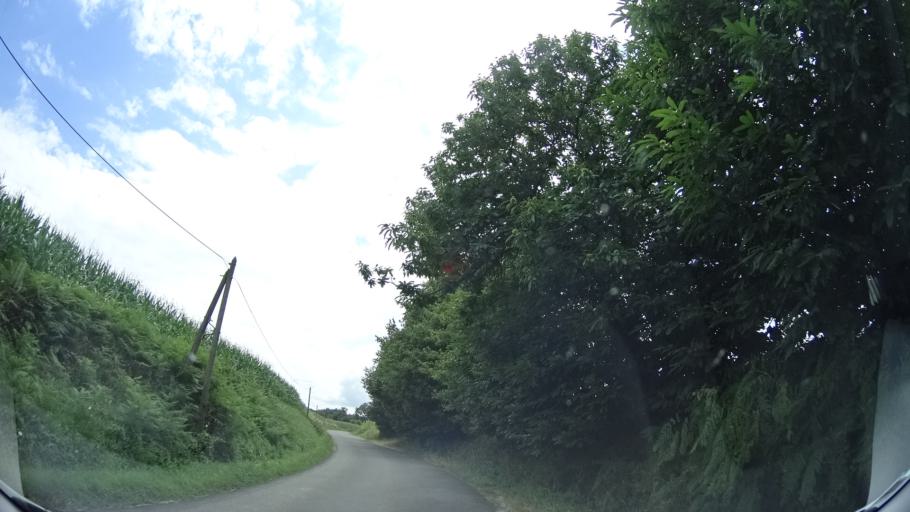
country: FR
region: Brittany
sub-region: Departement d'Ille-et-Vilaine
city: La Meziere
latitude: 48.1914
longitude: -1.7671
